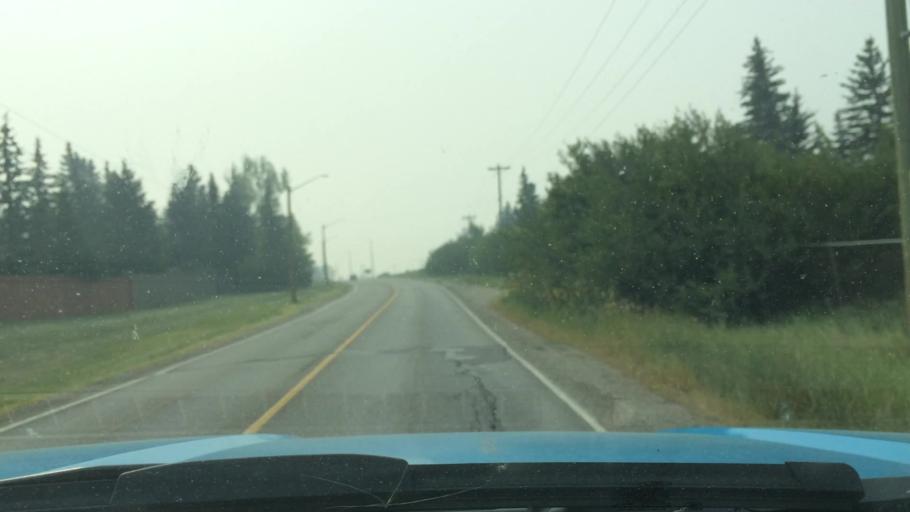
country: CA
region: Alberta
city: Calgary
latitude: 50.9440
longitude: -114.0948
